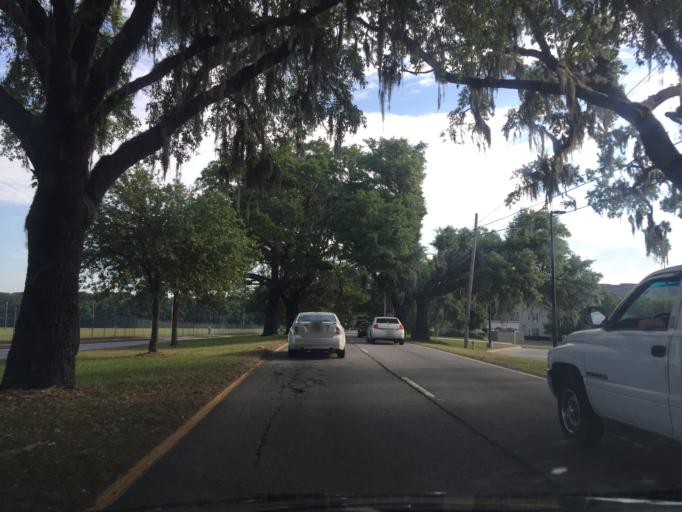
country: US
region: Georgia
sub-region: Chatham County
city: Isle of Hope
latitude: 32.0067
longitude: -81.1192
